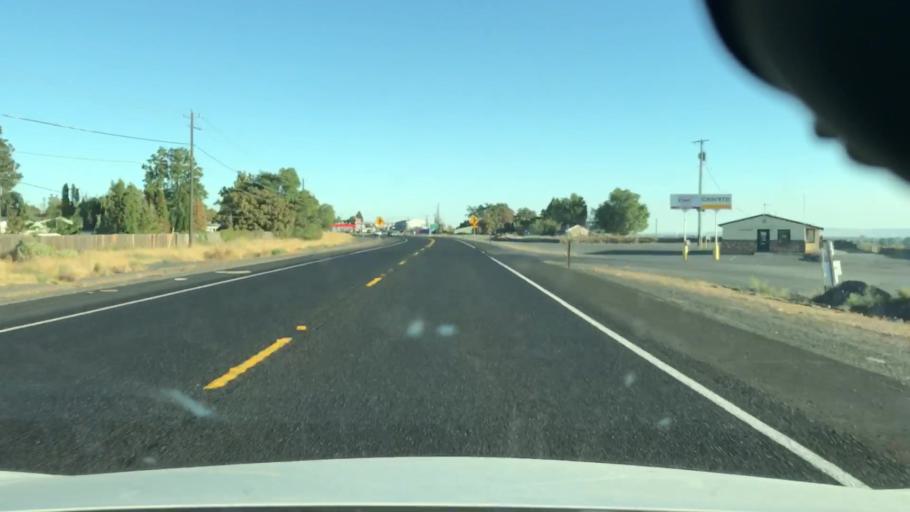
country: US
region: Washington
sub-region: Grant County
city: Moses Lake North
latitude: 47.1650
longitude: -119.3257
